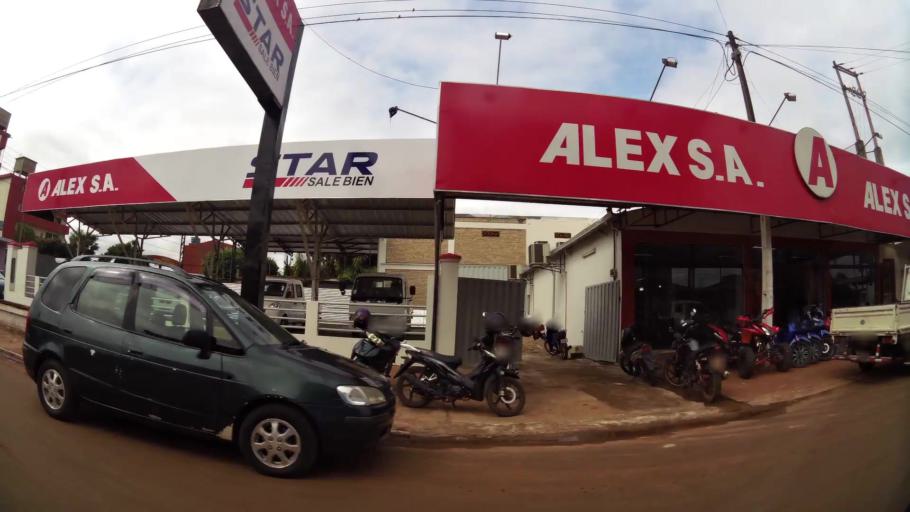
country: PY
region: Alto Parana
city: Ciudad del Este
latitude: -25.3925
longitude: -54.6417
